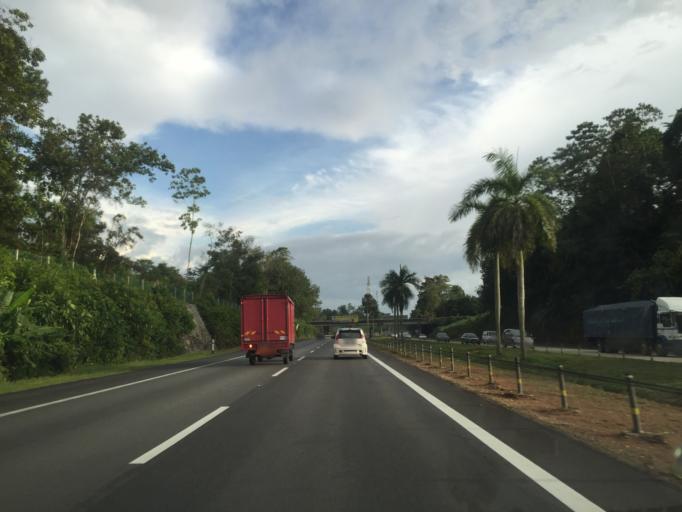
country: MY
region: Kedah
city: Gurun
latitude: 5.8557
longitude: 100.4823
